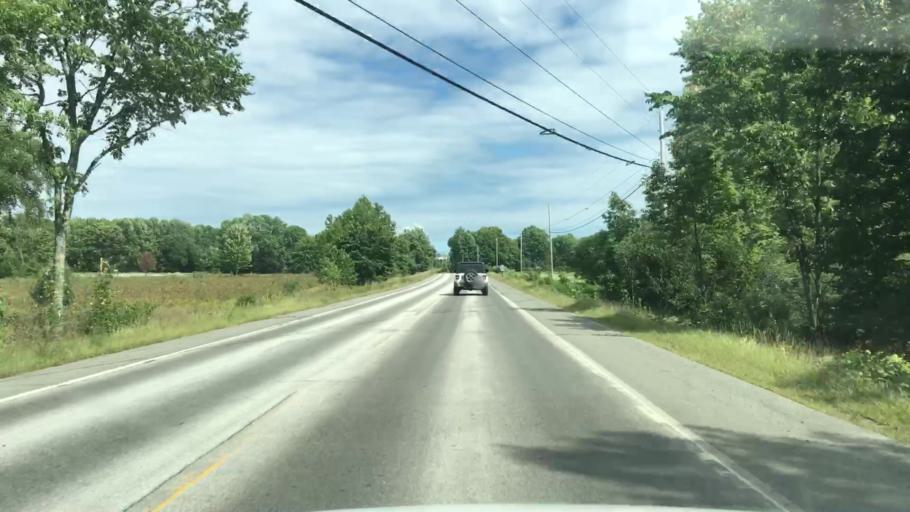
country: US
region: Maine
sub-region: Piscataquis County
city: Dover-Foxcroft
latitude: 45.1561
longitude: -69.2346
